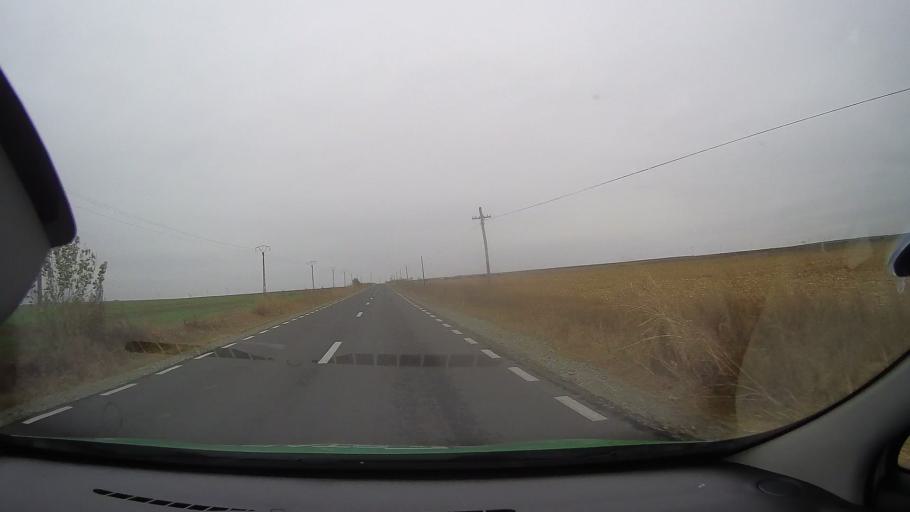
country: RO
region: Constanta
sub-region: Comuna Tortoman
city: Tortoman
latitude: 44.3526
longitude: 28.2152
